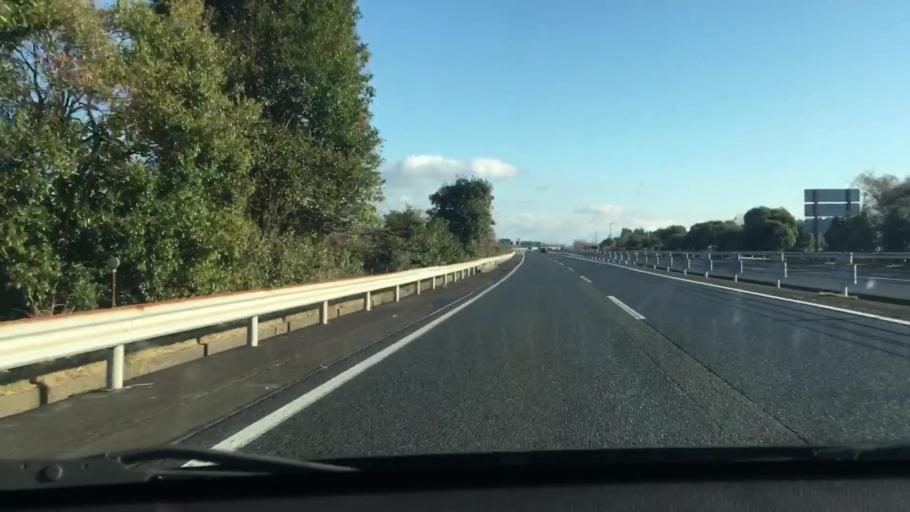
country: JP
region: Kagoshima
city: Kajiki
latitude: 31.8035
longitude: 130.7105
